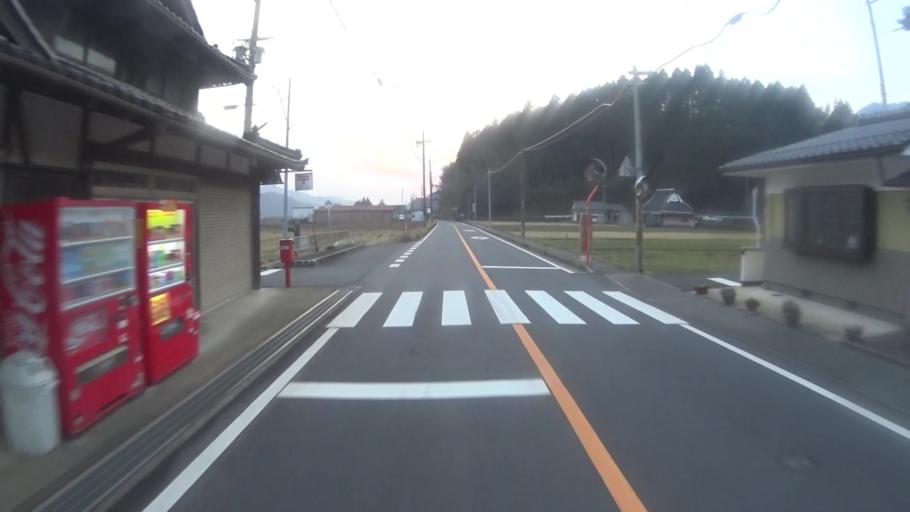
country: JP
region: Kyoto
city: Maizuru
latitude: 35.3676
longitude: 135.4130
